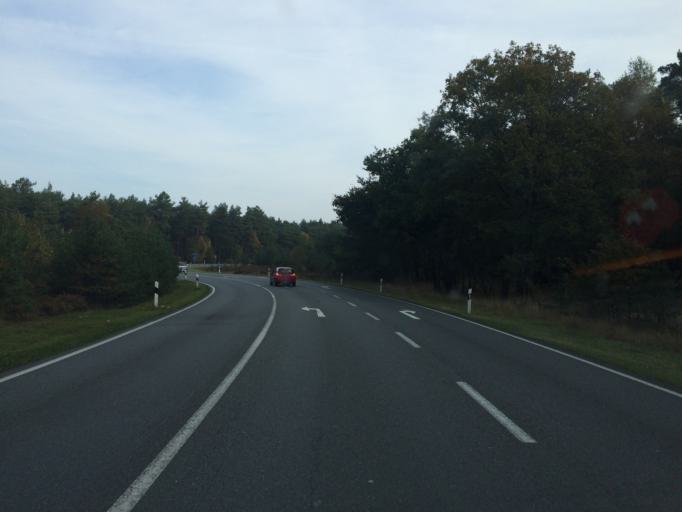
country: DE
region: Lower Saxony
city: Soltau
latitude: 52.9997
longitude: 9.9331
